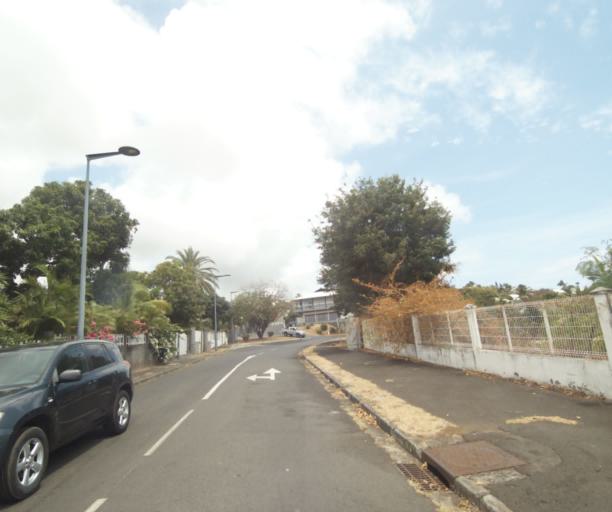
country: RE
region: Reunion
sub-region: Reunion
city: Saint-Paul
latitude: -21.0236
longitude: 55.2723
